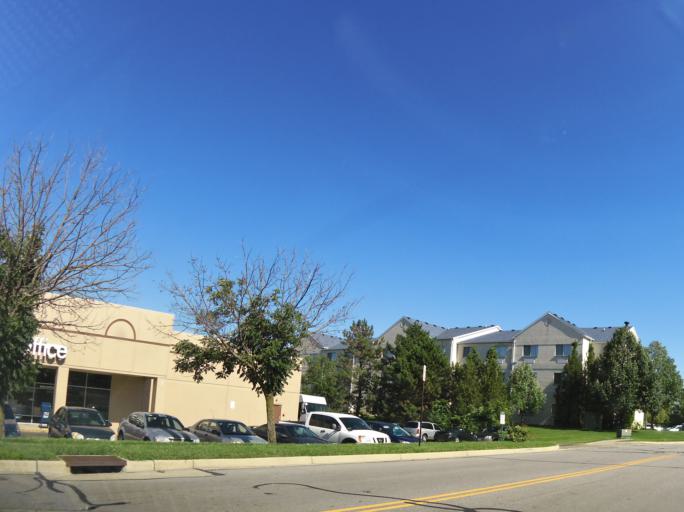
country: US
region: Ohio
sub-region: Greene County
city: Wright-Patterson AFB
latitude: 39.7779
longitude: -84.0555
